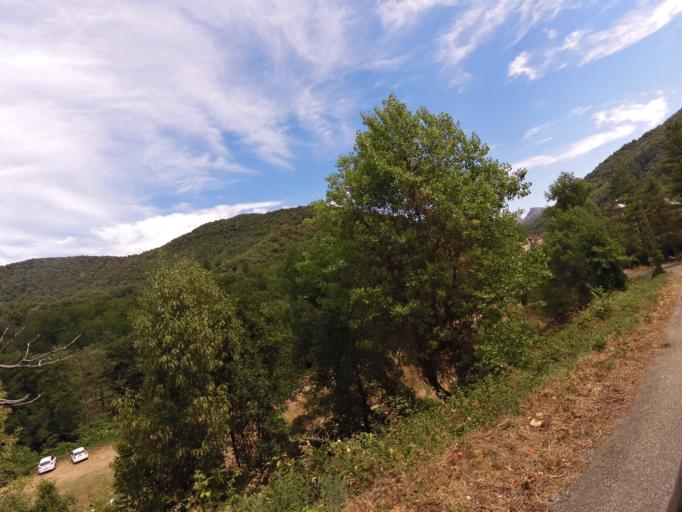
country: FR
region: Languedoc-Roussillon
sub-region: Departement du Gard
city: Sumene
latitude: 44.0013
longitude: 3.6591
